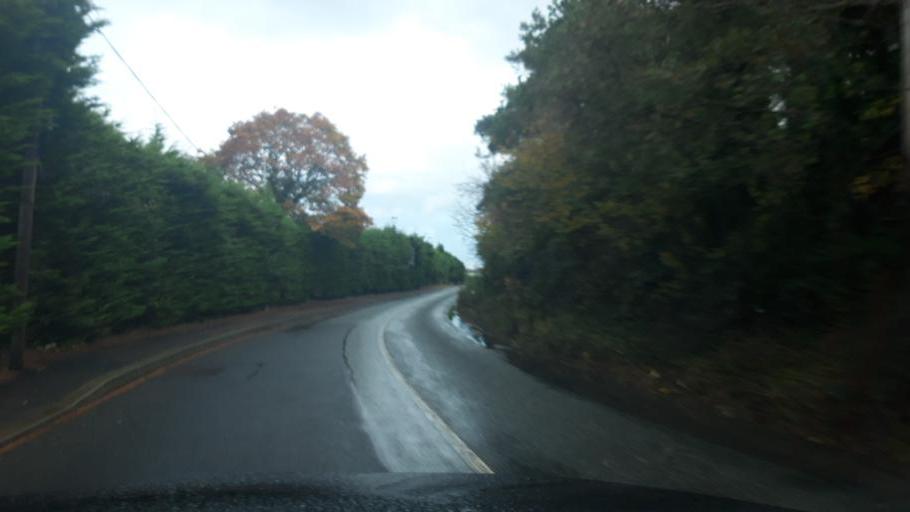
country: IE
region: Leinster
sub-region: Wicklow
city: Kilcoole
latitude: 53.0973
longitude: -6.0682
